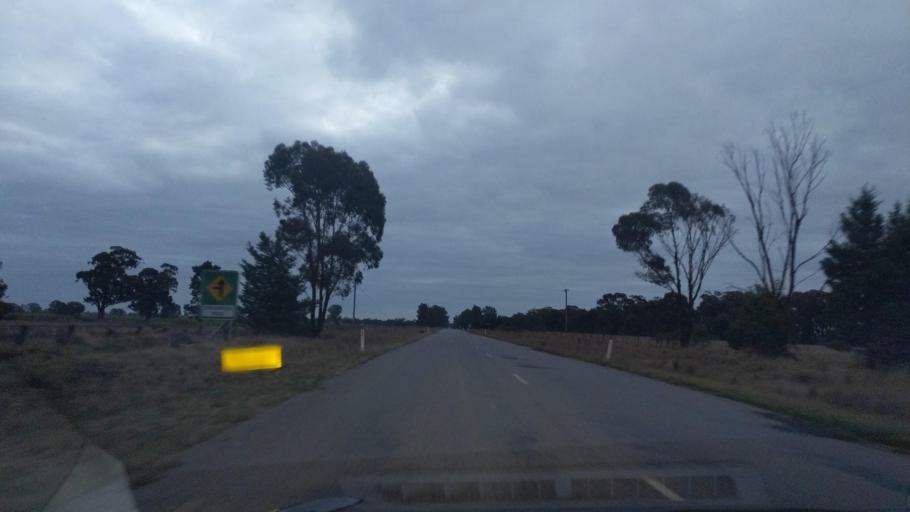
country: AU
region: New South Wales
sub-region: Narrandera
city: Narrandera
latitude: -34.7496
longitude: 146.8311
